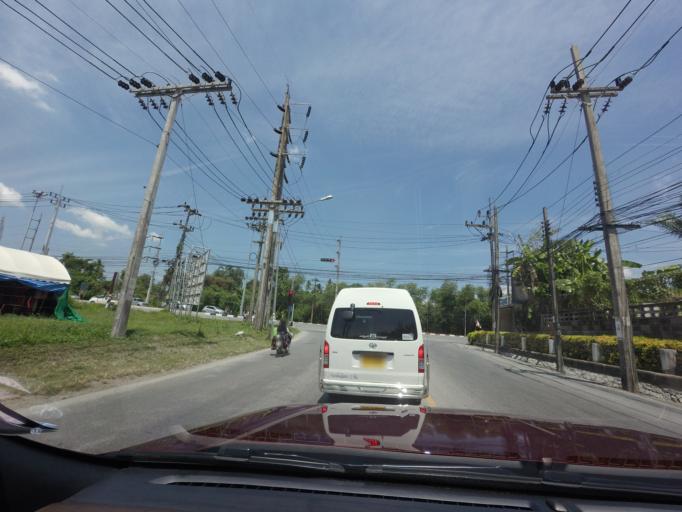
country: TH
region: Yala
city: Yala
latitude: 6.5530
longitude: 101.2706
